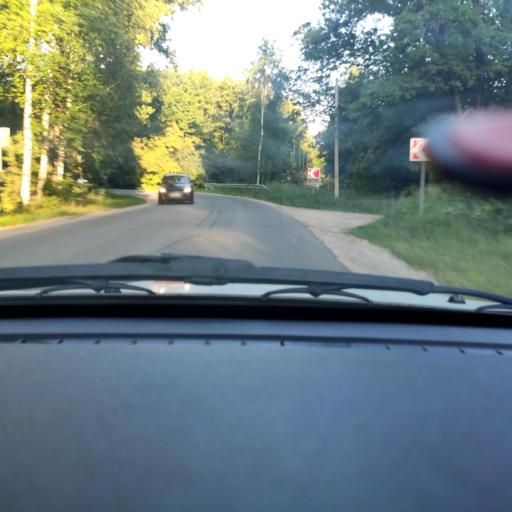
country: RU
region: Voronezj
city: Ramon'
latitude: 51.8939
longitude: 39.2805
